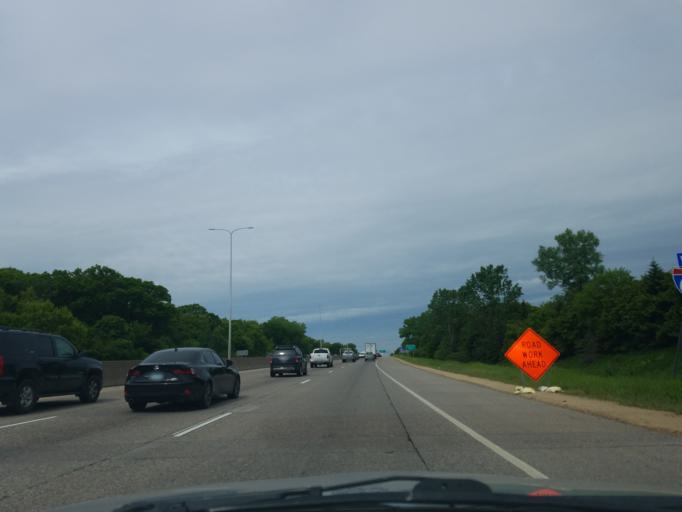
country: US
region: Minnesota
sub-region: Ramsey County
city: New Brighton
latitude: 45.0649
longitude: -93.2250
